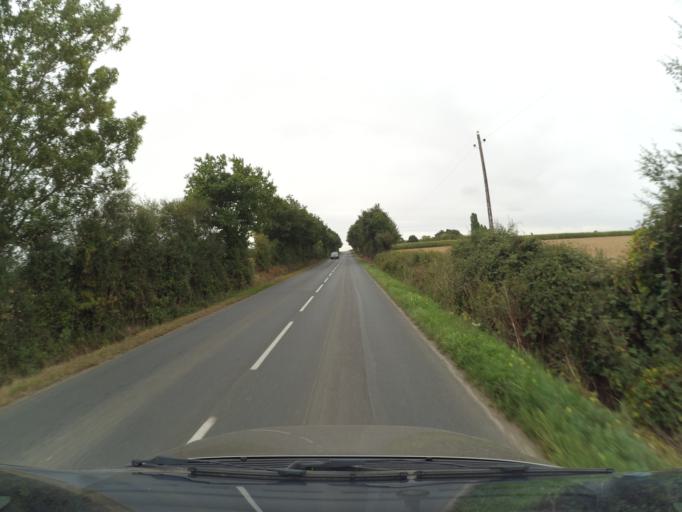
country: FR
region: Pays de la Loire
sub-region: Departement de la Vendee
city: Saint-Andre-Treize-Voies
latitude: 46.9280
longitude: -1.4003
